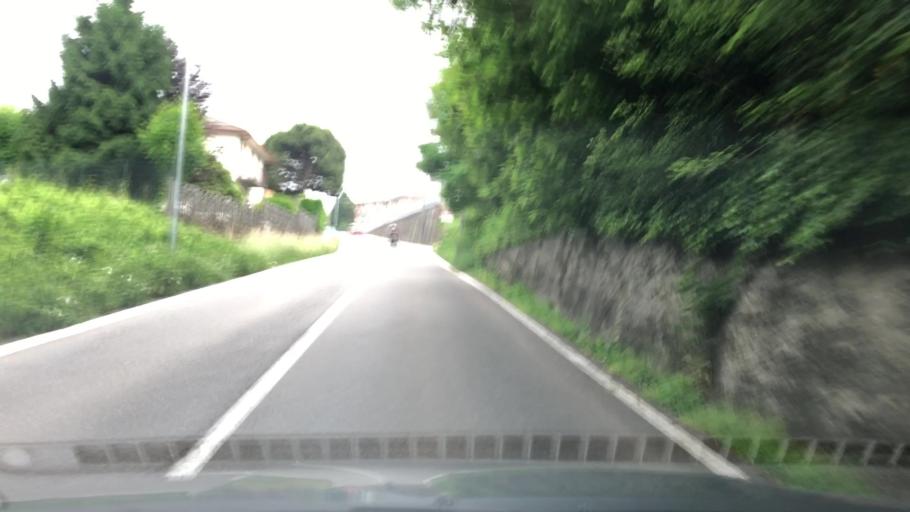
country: IT
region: Lombardy
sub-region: Provincia di Como
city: Casnate Con Bernate
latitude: 45.7649
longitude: 9.0743
